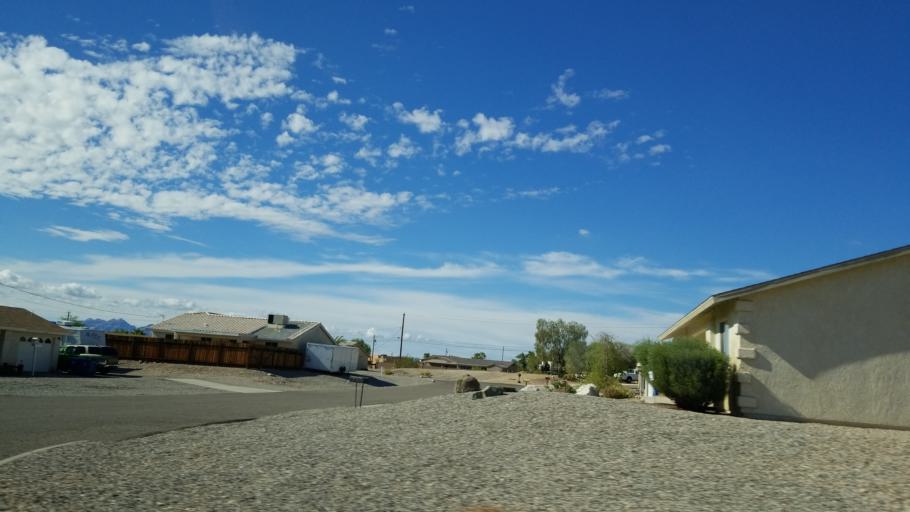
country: US
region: Arizona
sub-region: Mohave County
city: Lake Havasu City
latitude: 34.4947
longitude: -114.2904
